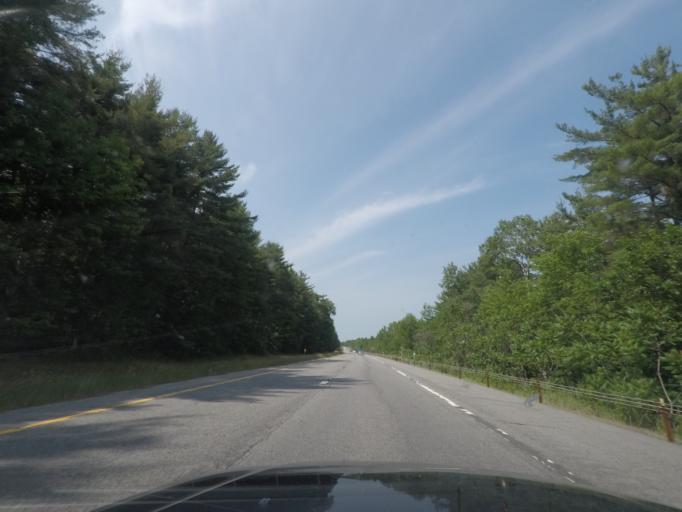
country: US
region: New York
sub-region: Essex County
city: Elizabethtown
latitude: 44.1404
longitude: -73.5843
